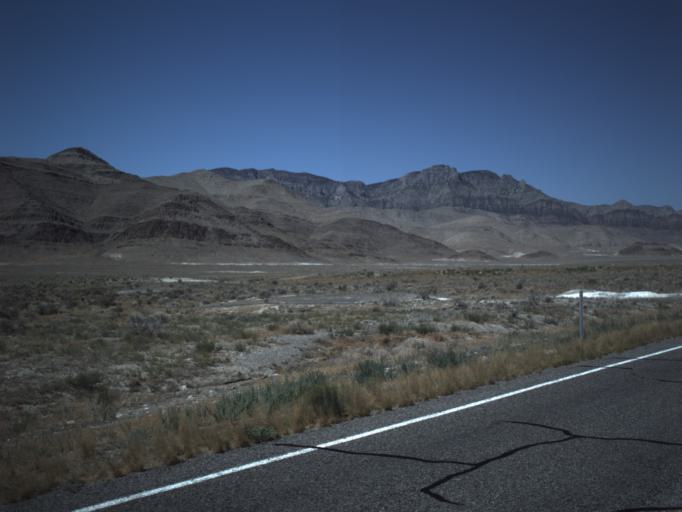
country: US
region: Utah
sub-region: Beaver County
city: Milford
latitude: 39.0375
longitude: -113.3948
